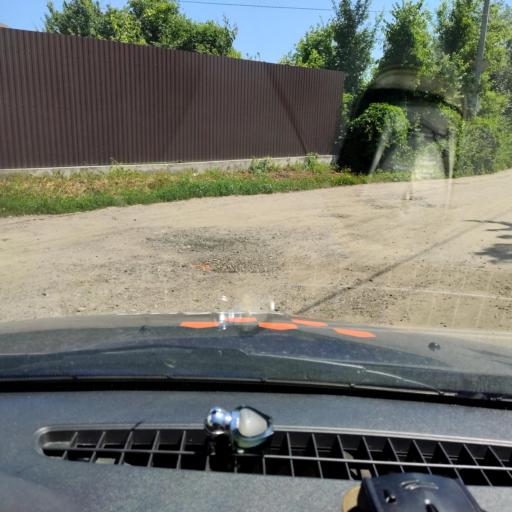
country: RU
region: Voronezj
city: Shilovo
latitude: 51.5963
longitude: 39.1289
